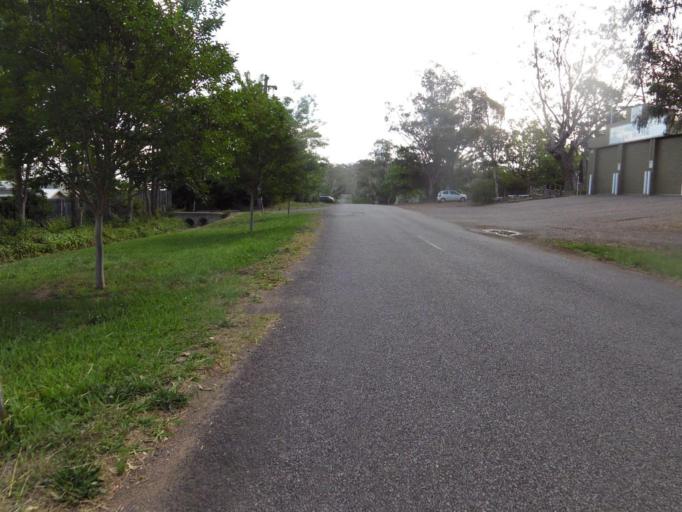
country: AU
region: Australian Capital Territory
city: Belconnen
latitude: -35.1689
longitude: 149.0703
